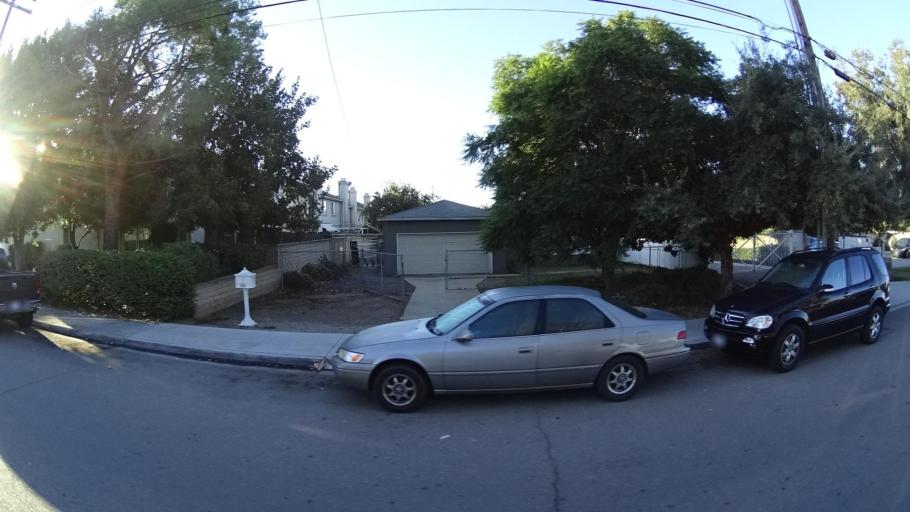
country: US
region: California
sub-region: San Diego County
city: Bostonia
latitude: 32.8098
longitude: -116.9390
